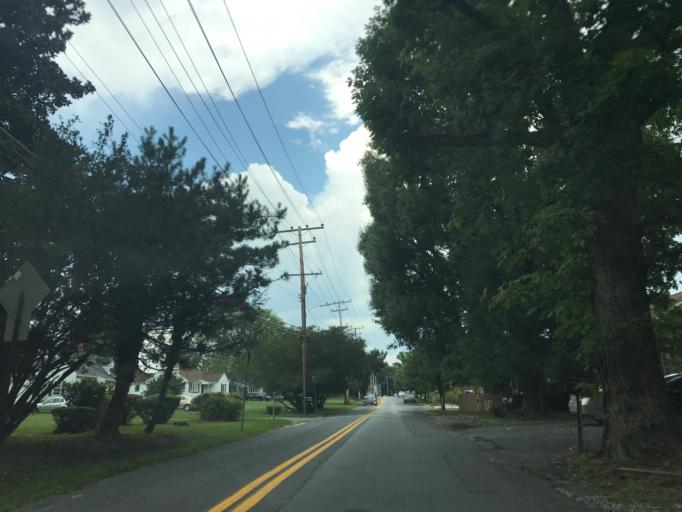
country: US
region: Maryland
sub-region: Baltimore County
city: Lochearn
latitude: 39.3450
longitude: -76.7252
